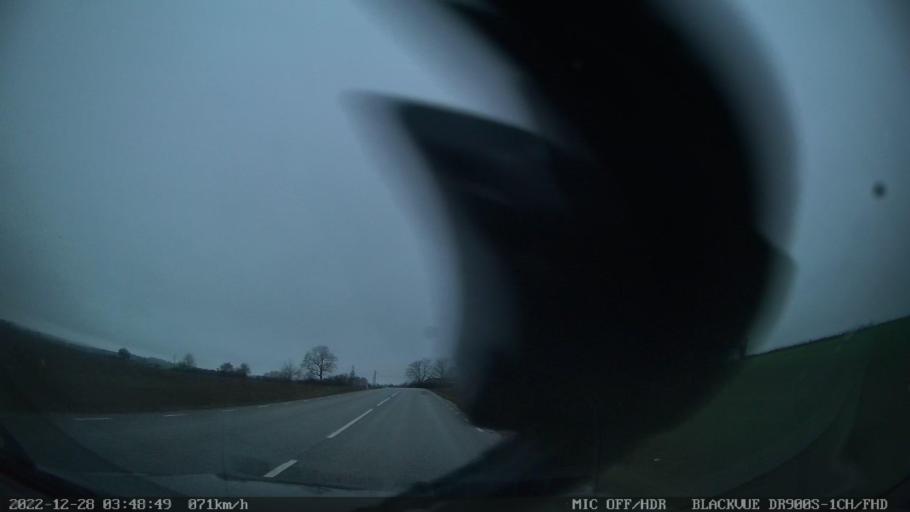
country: SE
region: Skane
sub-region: Tomelilla Kommun
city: Tomelilla
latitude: 55.5252
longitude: 13.9195
